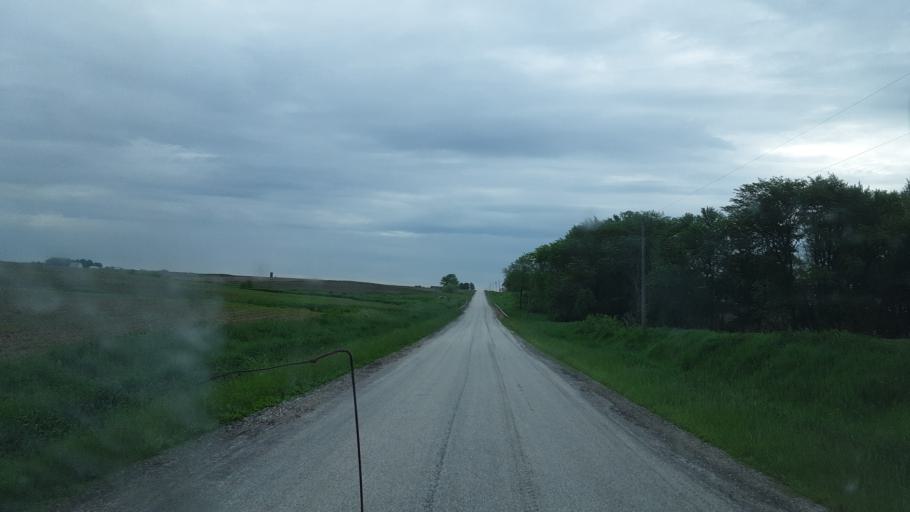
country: US
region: Illinois
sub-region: McDonough County
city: Macomb
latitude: 40.3820
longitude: -90.6474
